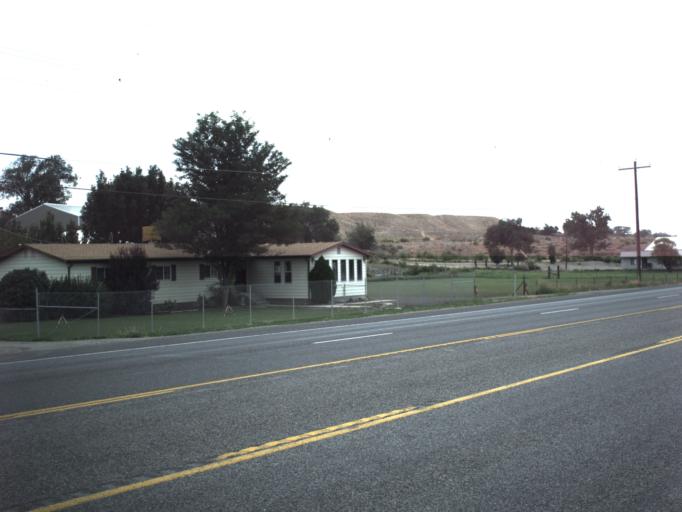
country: US
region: Utah
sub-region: Carbon County
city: Wellington
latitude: 39.5543
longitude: -110.7584
